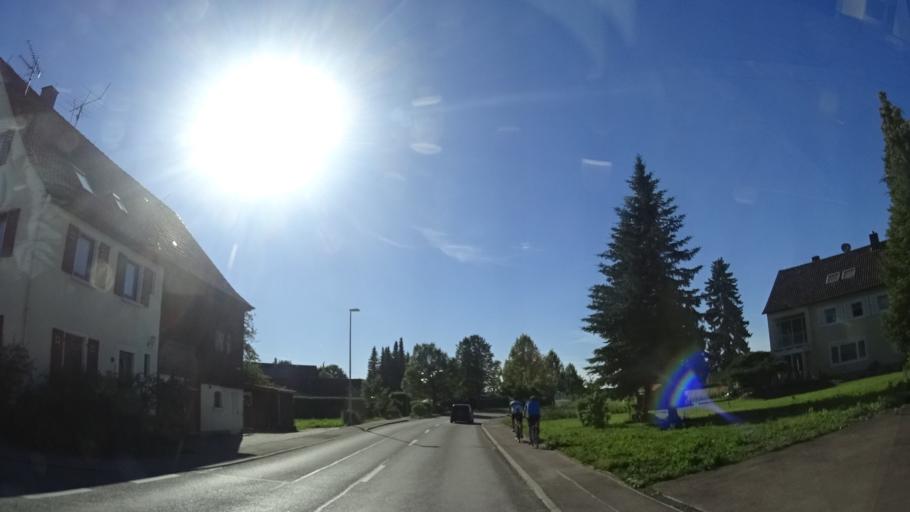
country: DE
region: Baden-Wuerttemberg
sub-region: Regierungsbezirk Stuttgart
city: Buhlertann
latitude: 49.0413
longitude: 9.9032
